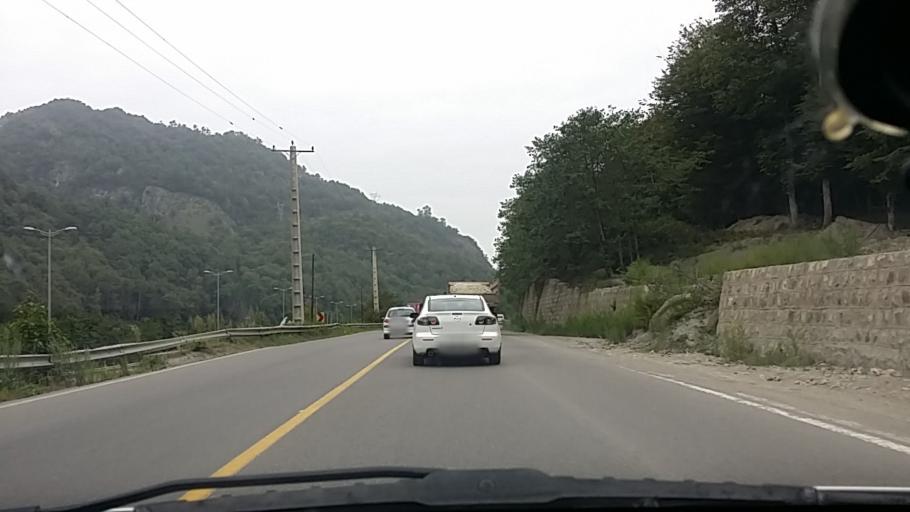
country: IR
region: Mazandaran
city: Chalus
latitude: 36.5633
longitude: 51.3760
